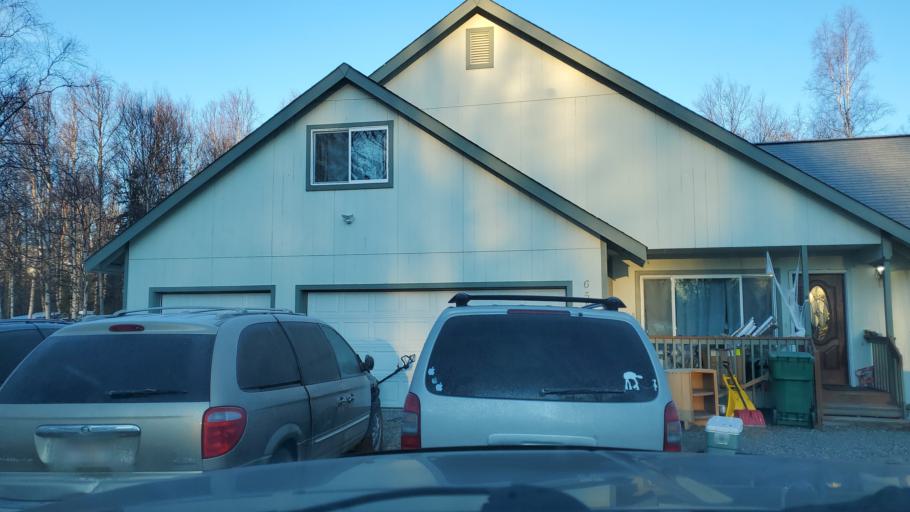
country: US
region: Alaska
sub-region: Matanuska-Susitna Borough
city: Lakes
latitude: 61.6601
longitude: -149.2866
